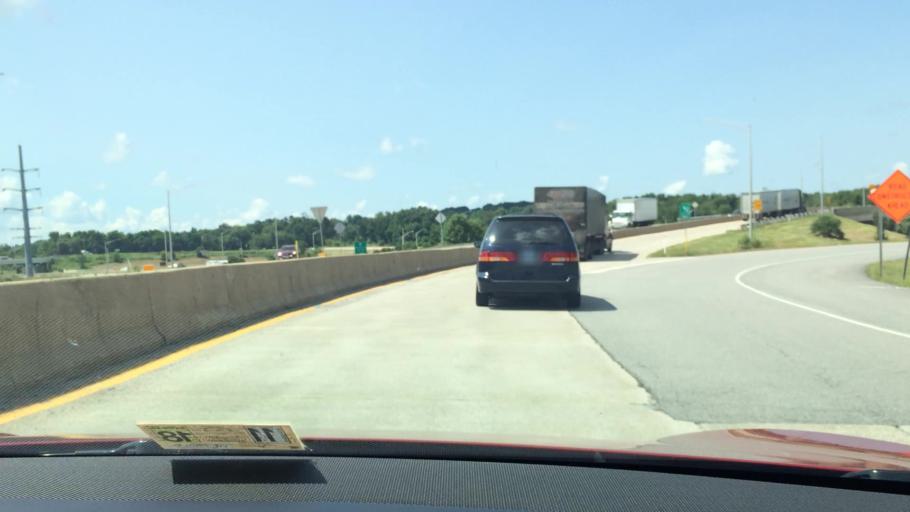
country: US
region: Indiana
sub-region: Saint Joseph County
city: South Bend
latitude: 41.7265
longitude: -86.3372
